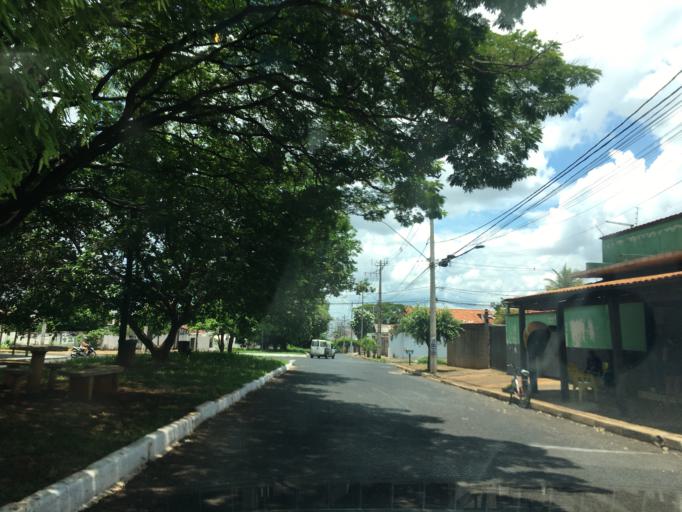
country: BR
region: Minas Gerais
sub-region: Uberlandia
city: Uberlandia
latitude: -18.9329
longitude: -48.3061
